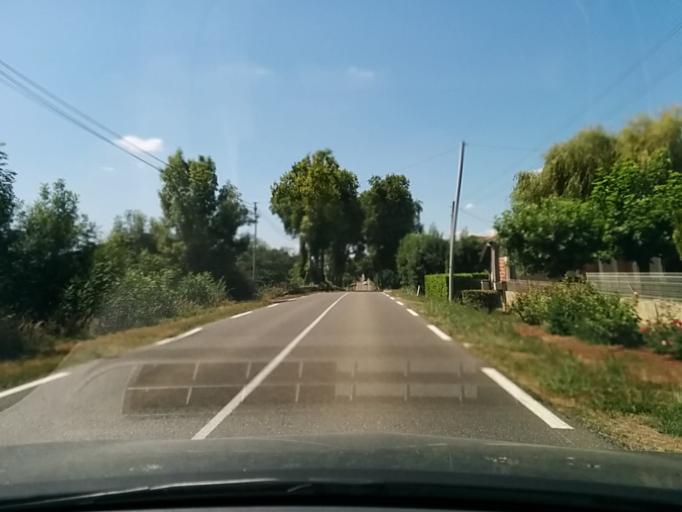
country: FR
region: Midi-Pyrenees
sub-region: Departement du Gers
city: Le Houga
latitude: 43.7622
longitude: -0.1103
